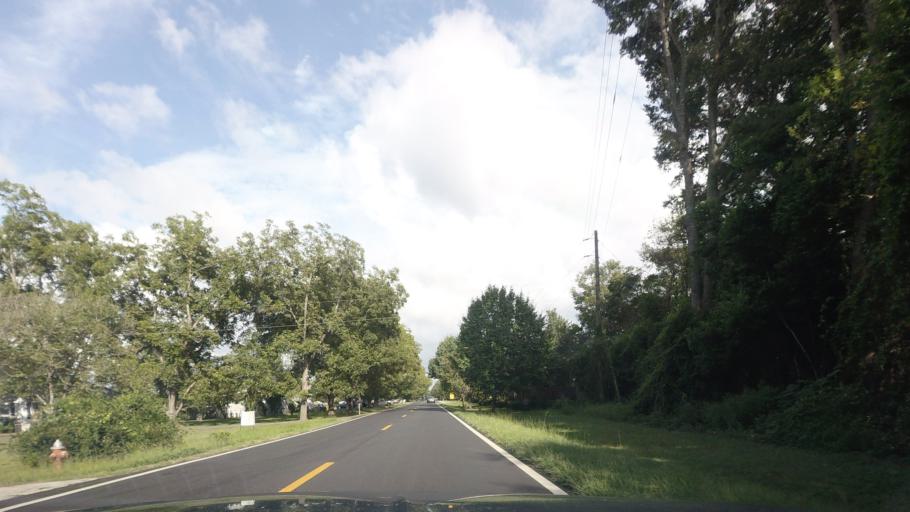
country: US
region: Georgia
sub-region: Houston County
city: Centerville
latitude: 32.6350
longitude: -83.7238
